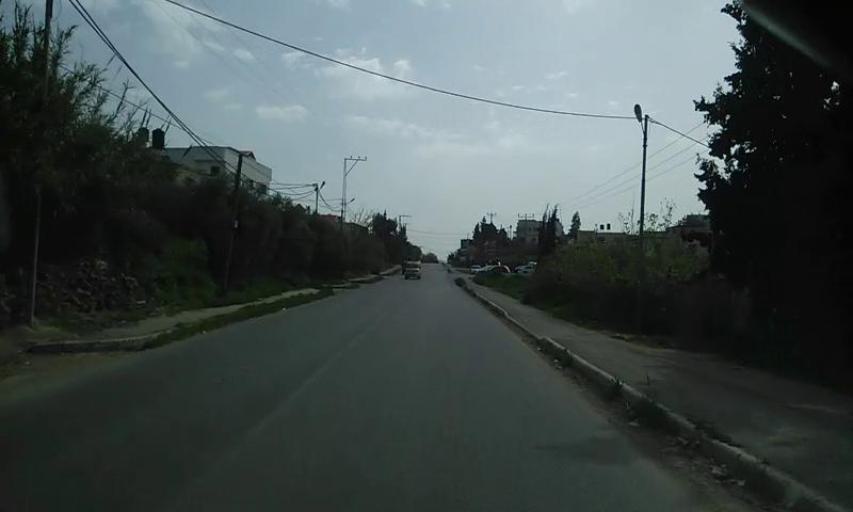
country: PS
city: Bir al Basha
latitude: 32.4216
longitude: 35.2314
